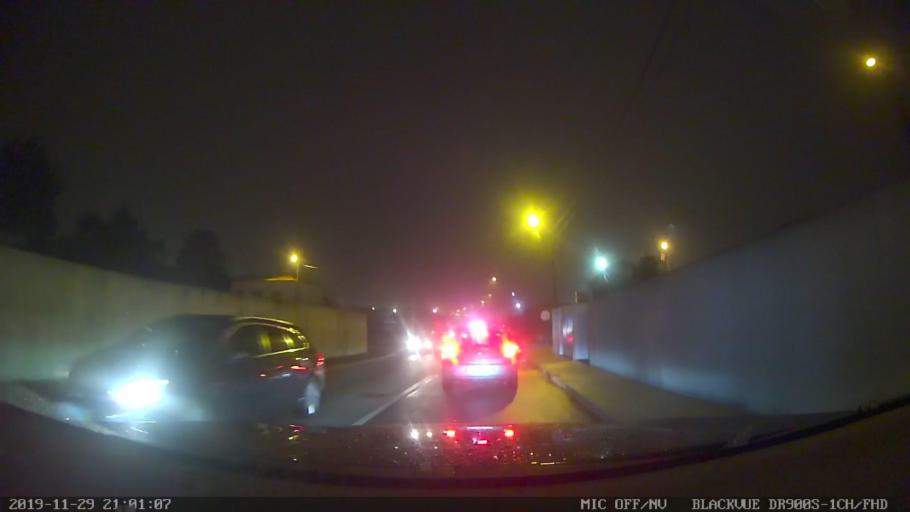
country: PT
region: Porto
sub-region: Matosinhos
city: Guifoes
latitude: 41.2101
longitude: -8.6769
